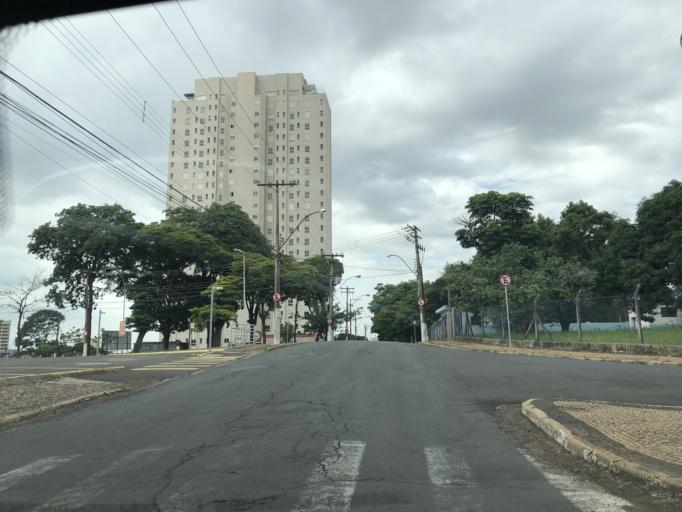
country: BR
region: Sao Paulo
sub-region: Americana
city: Americana
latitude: -22.7410
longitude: -47.3358
